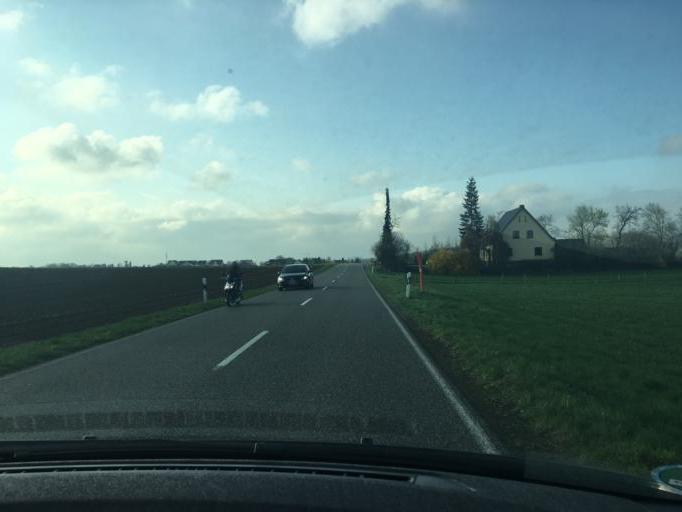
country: DE
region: North Rhine-Westphalia
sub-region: Regierungsbezirk Koln
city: Weilerswist
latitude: 50.7270
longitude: 6.9003
